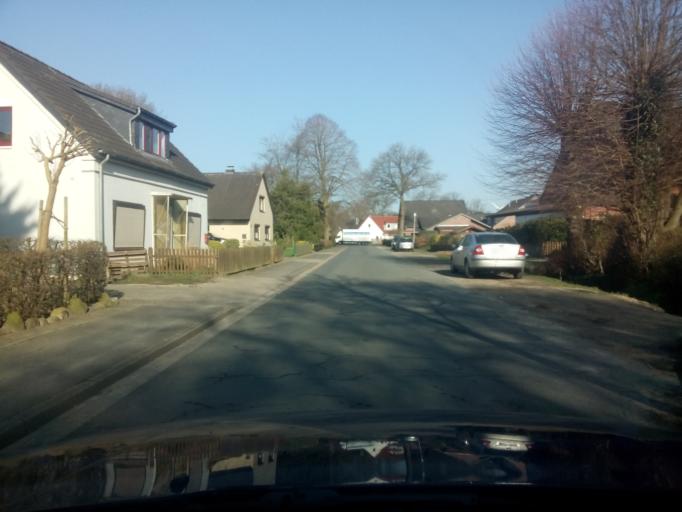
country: DE
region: Lower Saxony
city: Osterholz-Scharmbeck
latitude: 53.2262
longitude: 8.7620
